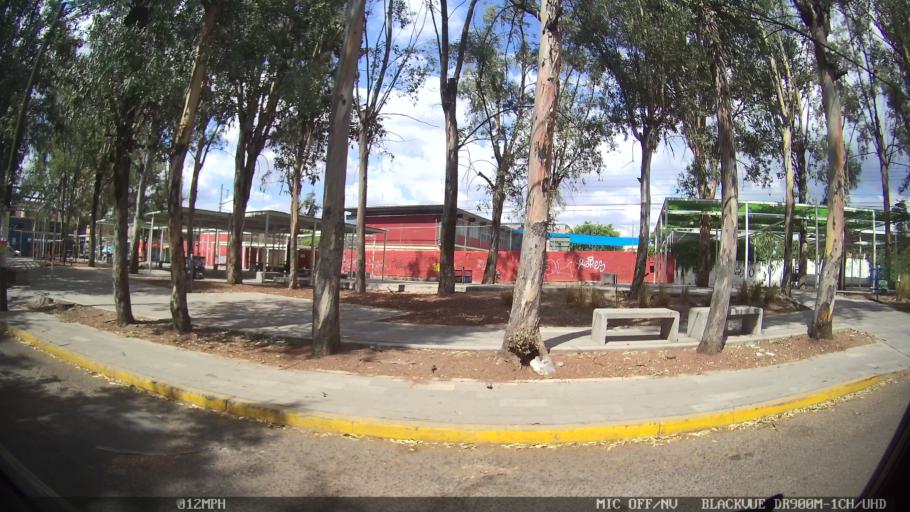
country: MX
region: Jalisco
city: Tlaquepaque
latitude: 20.6846
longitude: -103.2641
